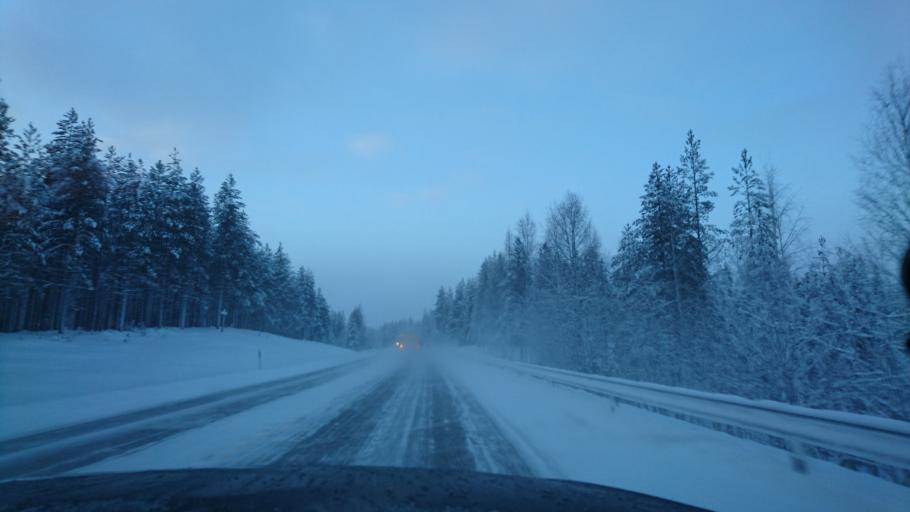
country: FI
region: Northern Ostrobothnia
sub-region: Koillismaa
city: Taivalkoski
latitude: 65.4845
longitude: 27.8151
